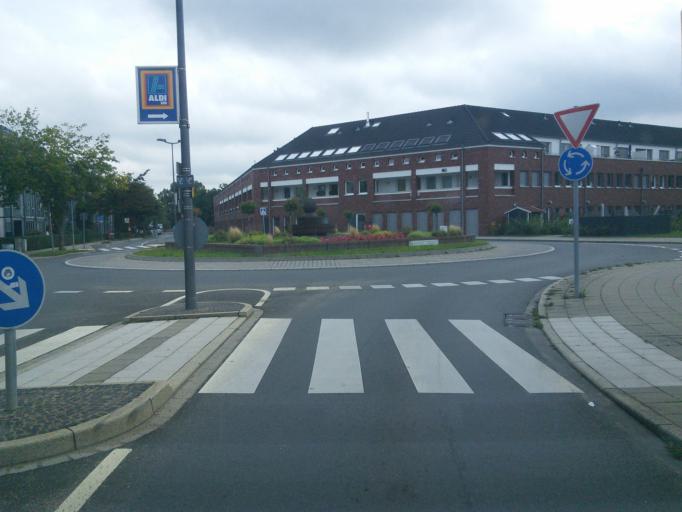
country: DE
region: North Rhine-Westphalia
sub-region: Regierungsbezirk Koln
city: Mengenich
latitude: 50.9679
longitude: 6.8403
